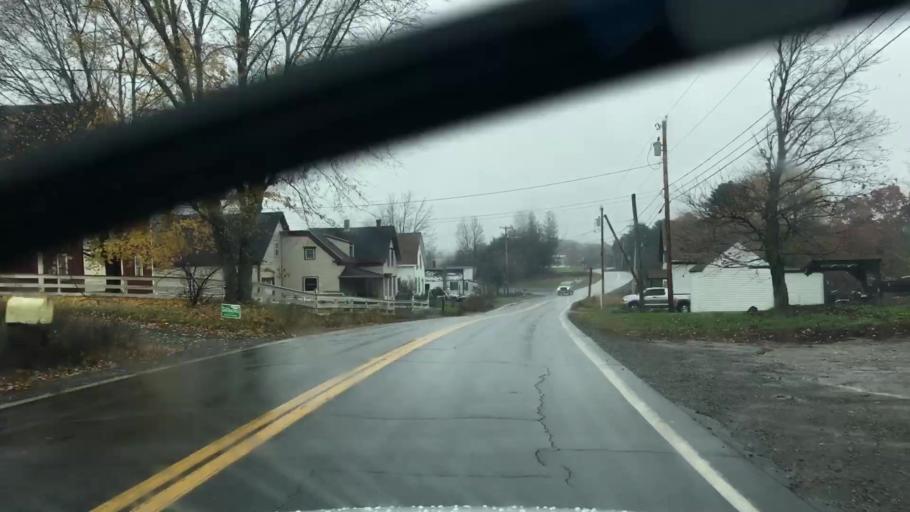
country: US
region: Maine
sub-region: Lincoln County
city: Waldoboro
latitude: 44.1194
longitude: -69.4098
